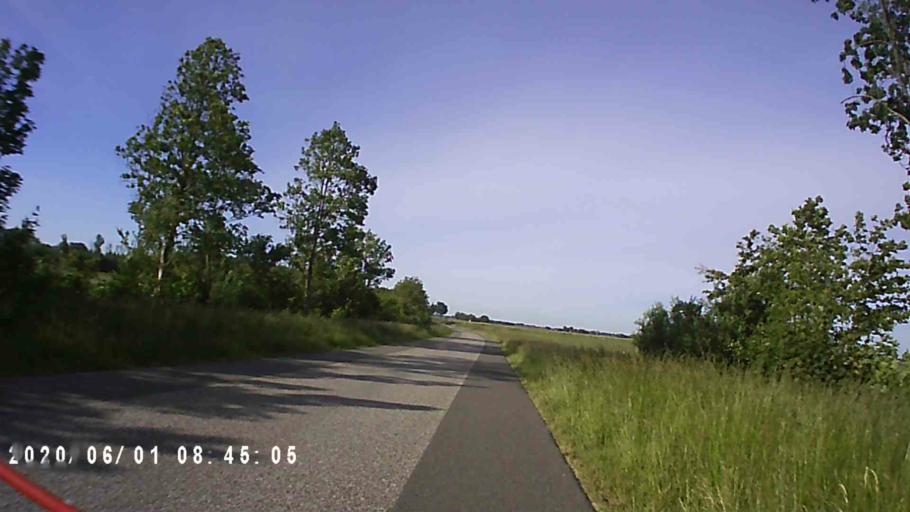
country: NL
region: Friesland
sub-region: Gemeente Ferwerderadiel
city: Burdaard
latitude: 53.2785
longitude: 5.8359
